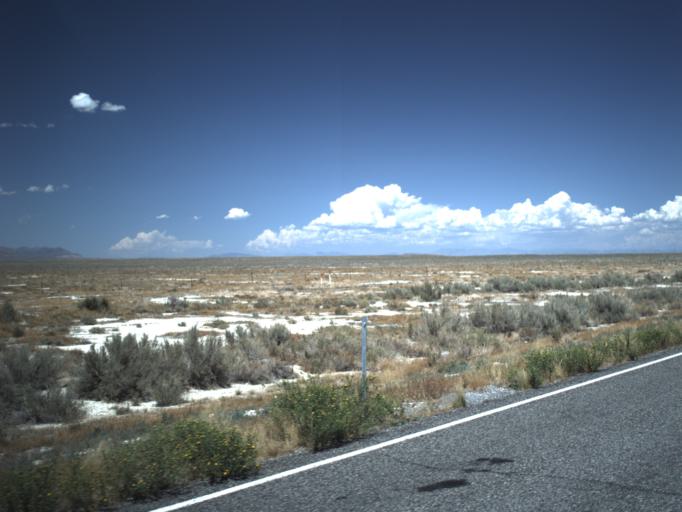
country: US
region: Utah
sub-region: Millard County
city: Delta
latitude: 39.2131
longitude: -112.9615
